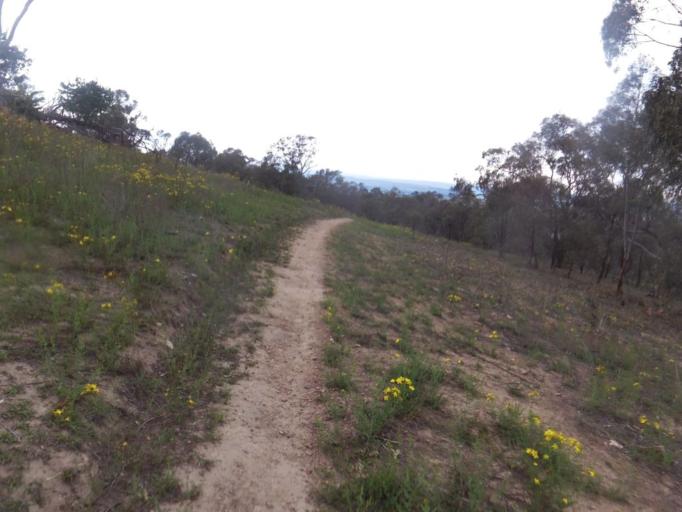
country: AU
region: Australian Capital Territory
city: Forrest
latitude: -35.3476
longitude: 149.1317
